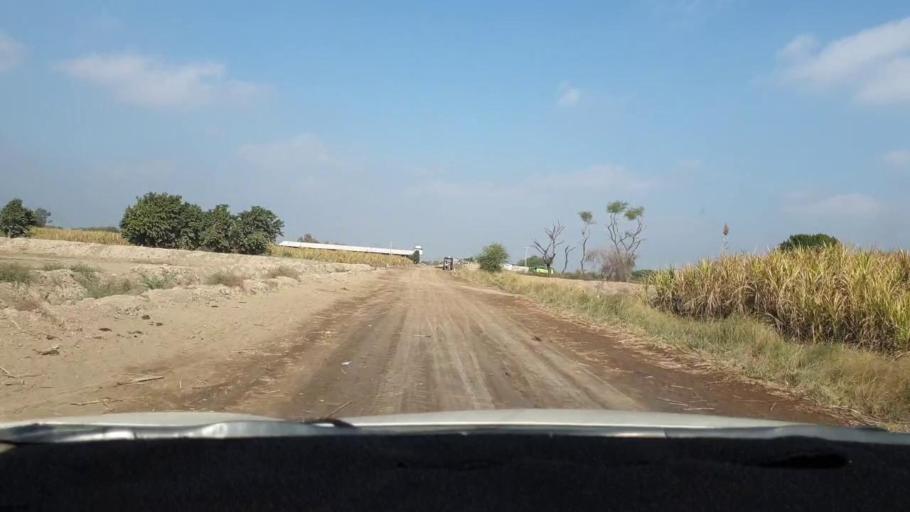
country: PK
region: Sindh
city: Berani
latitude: 25.7521
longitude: 69.0074
